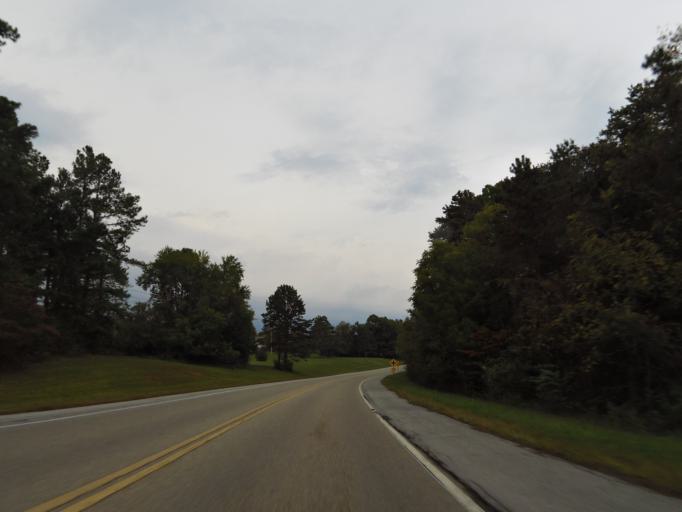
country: US
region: Tennessee
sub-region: Loudon County
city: Loudon
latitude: 35.6905
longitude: -84.2627
